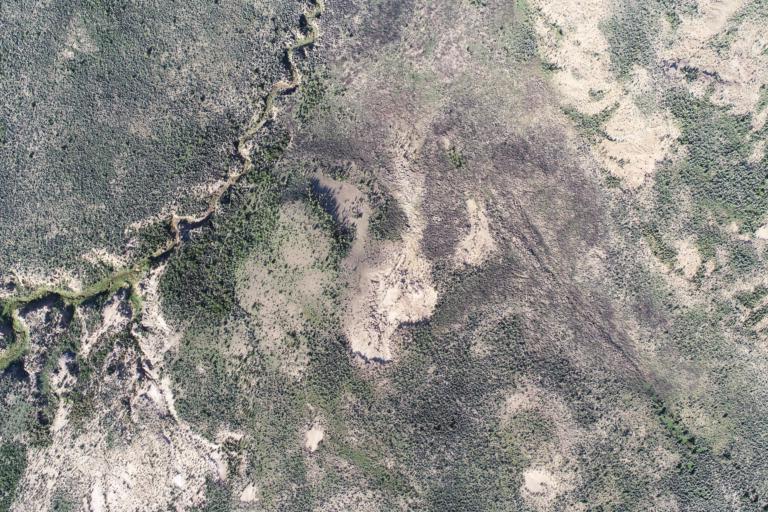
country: BO
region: La Paz
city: Curahuara de Carangas
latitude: -17.3008
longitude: -68.5137
